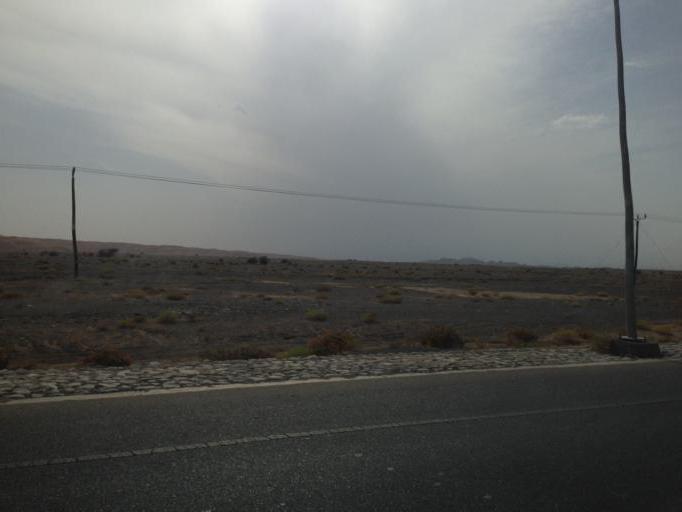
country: OM
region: Ash Sharqiyah
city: Al Qabil
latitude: 22.5157
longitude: 58.7377
